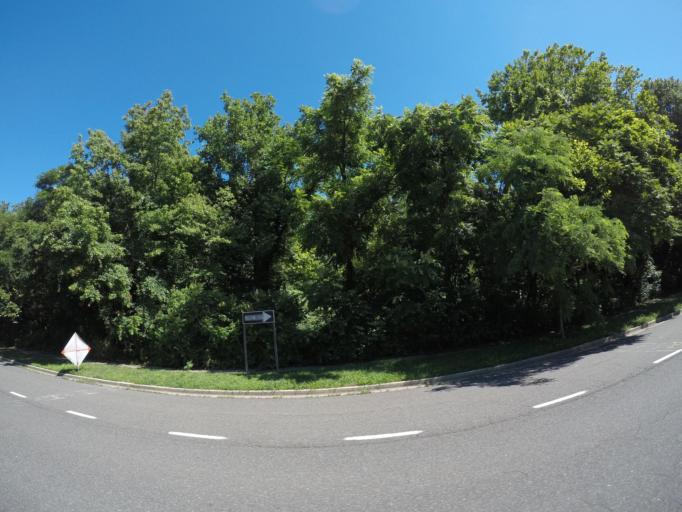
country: US
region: Maryland
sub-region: Prince George's County
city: Largo
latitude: 38.8953
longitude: -76.8421
